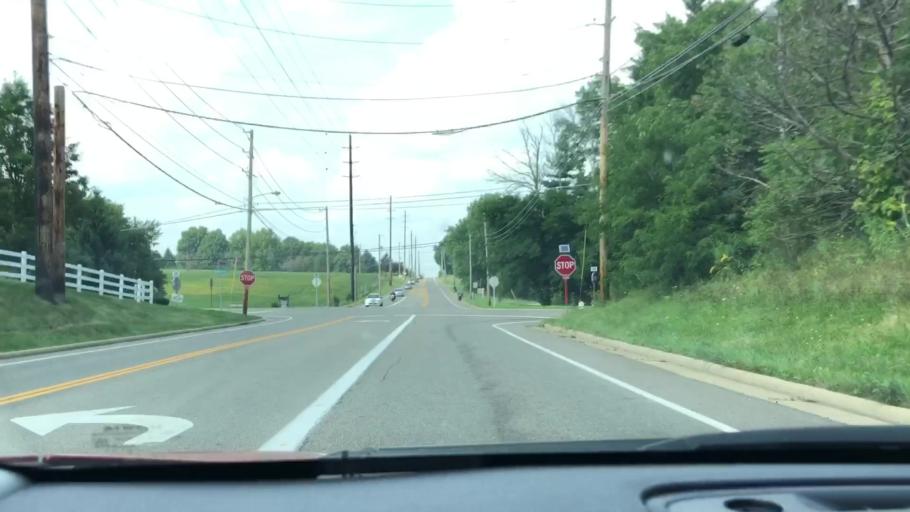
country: US
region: Ohio
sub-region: Summit County
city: Greensburg
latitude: 40.8715
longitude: -81.4999
